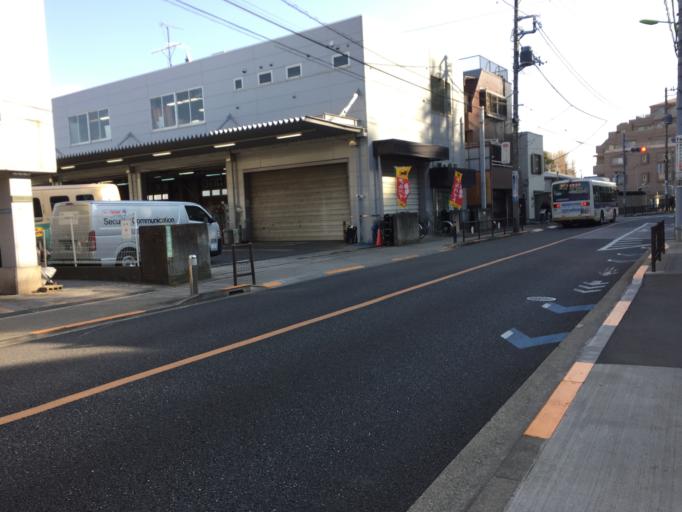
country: JP
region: Tokyo
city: Mitaka-shi
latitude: 35.6584
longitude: 139.6092
